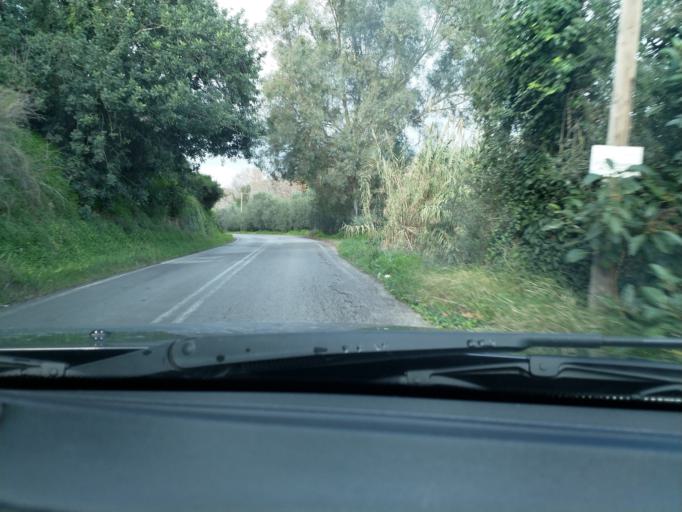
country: GR
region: Crete
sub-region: Nomos Chanias
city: Agia Marina
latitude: 35.4947
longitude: 23.9062
